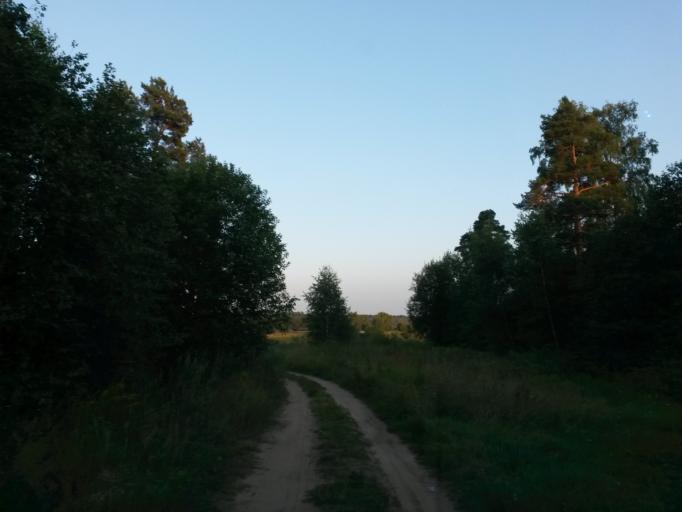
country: RU
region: Jaroslavl
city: Tutayev
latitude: 57.9348
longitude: 39.4466
